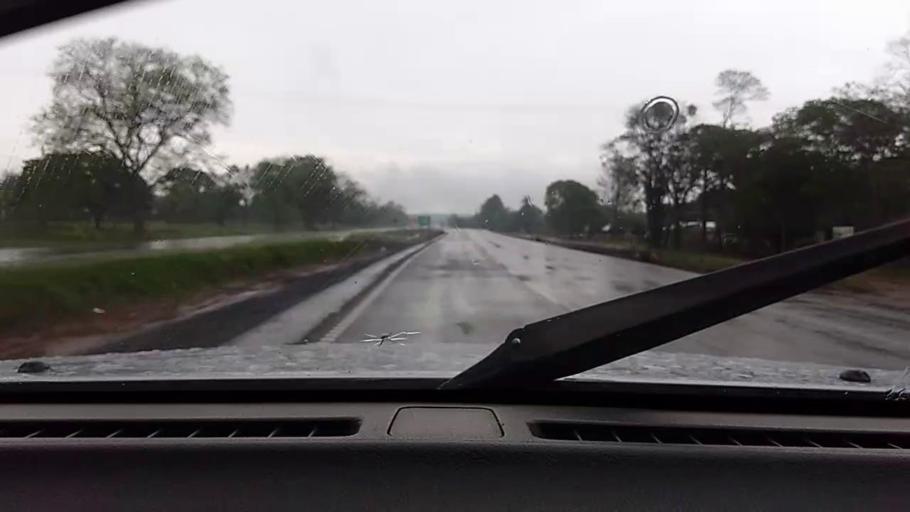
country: PY
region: Caaguazu
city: Repatriacion
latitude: -25.4595
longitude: -55.9217
